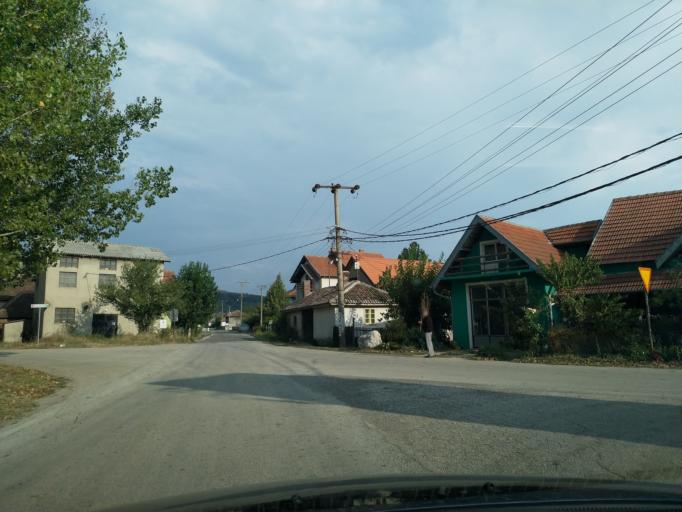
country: RS
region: Central Serbia
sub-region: Pomoravski Okrug
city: Paracin
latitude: 43.8217
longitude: 21.5396
